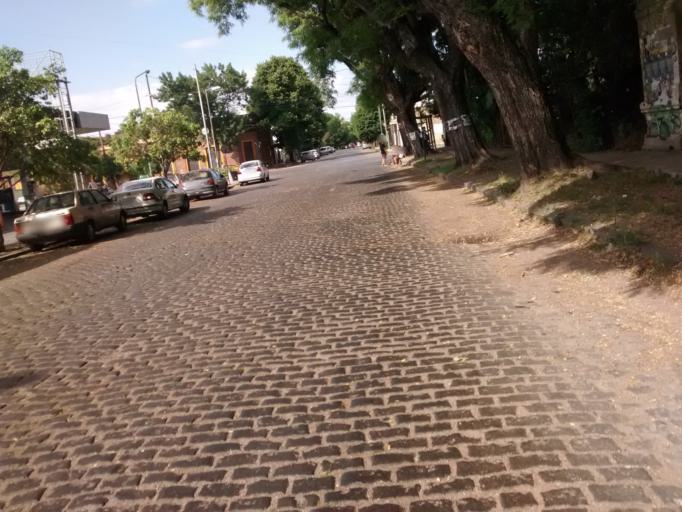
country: AR
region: Buenos Aires
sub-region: Partido de La Plata
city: La Plata
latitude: -34.9363
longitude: -57.9357
